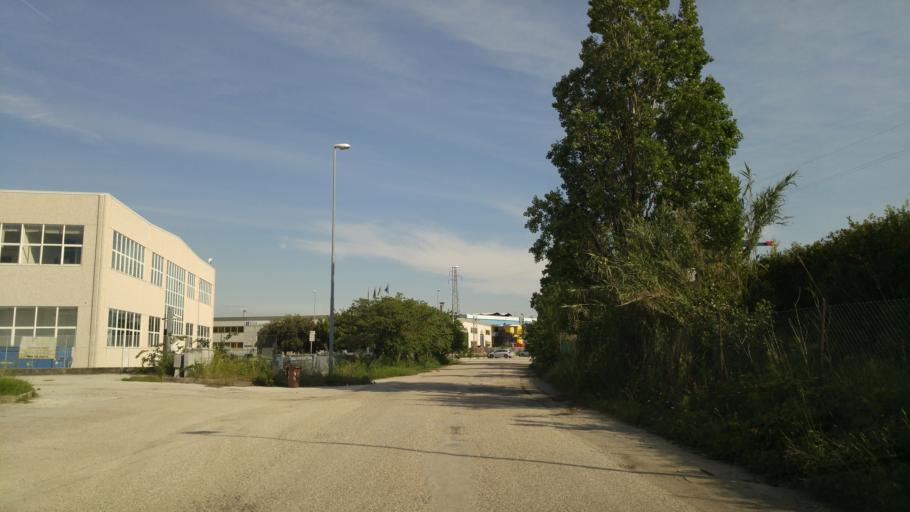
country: IT
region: The Marches
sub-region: Provincia di Pesaro e Urbino
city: Bellocchi
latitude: 43.7949
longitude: 13.0114
